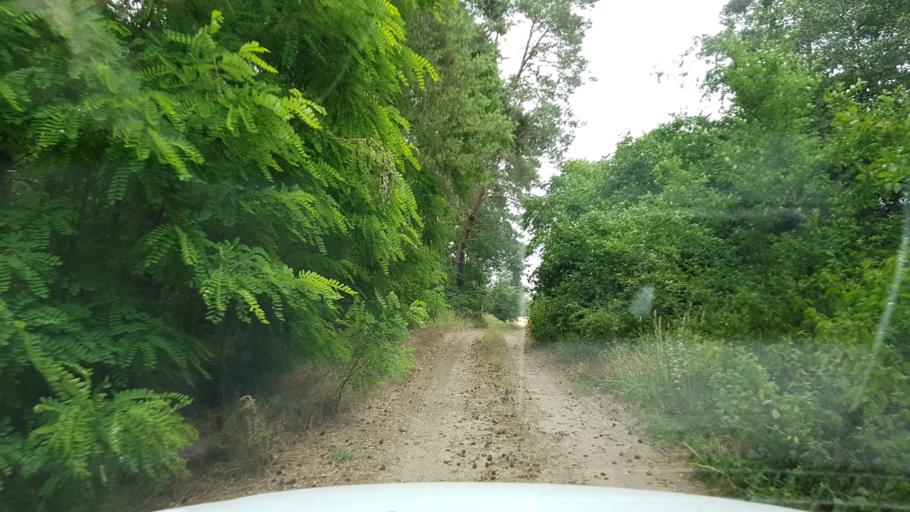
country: PL
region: West Pomeranian Voivodeship
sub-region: Powiat mysliborski
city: Mysliborz
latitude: 52.9372
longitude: 14.8925
